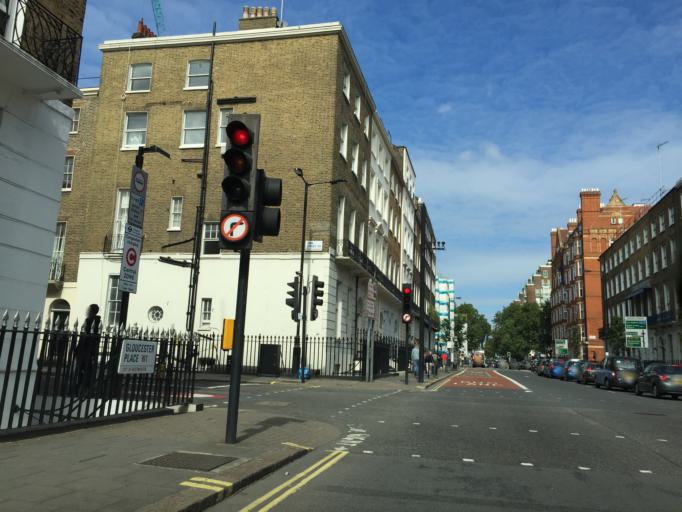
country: GB
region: England
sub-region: Greater London
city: Camden Town
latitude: 51.5204
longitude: -0.1590
